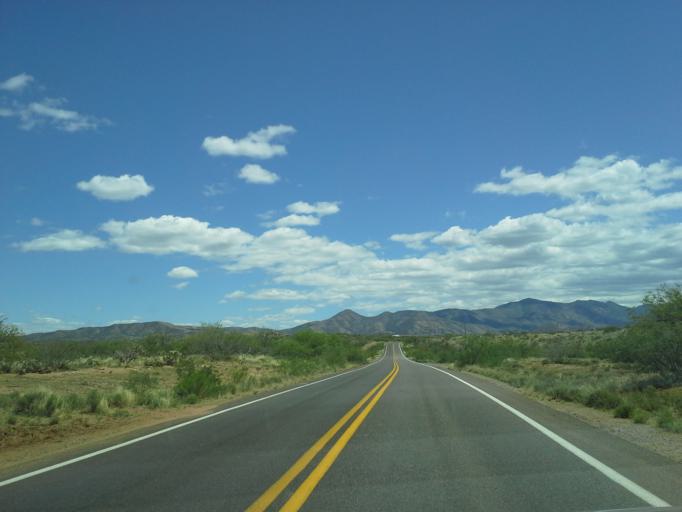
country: US
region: Arizona
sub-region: Pinal County
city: Oracle
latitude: 32.6033
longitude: -110.8601
